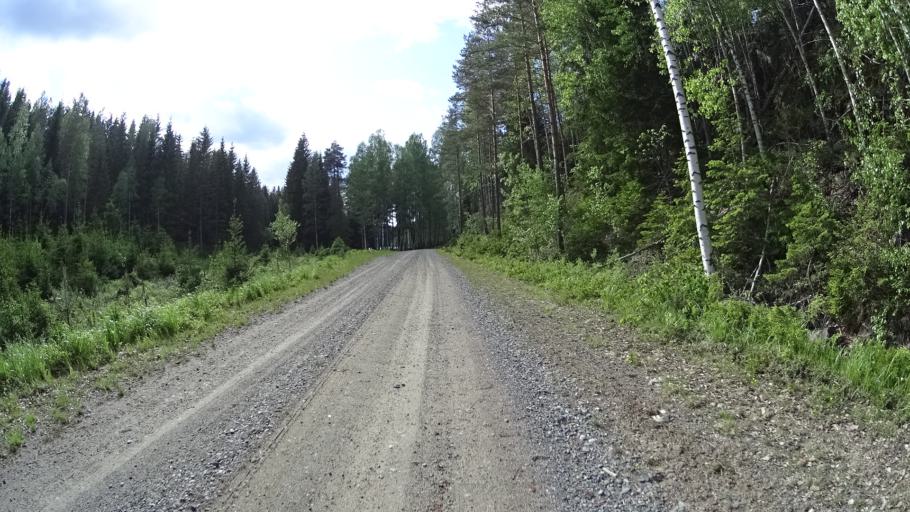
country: FI
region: Varsinais-Suomi
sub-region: Salo
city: Kisko
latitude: 60.1804
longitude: 23.5096
